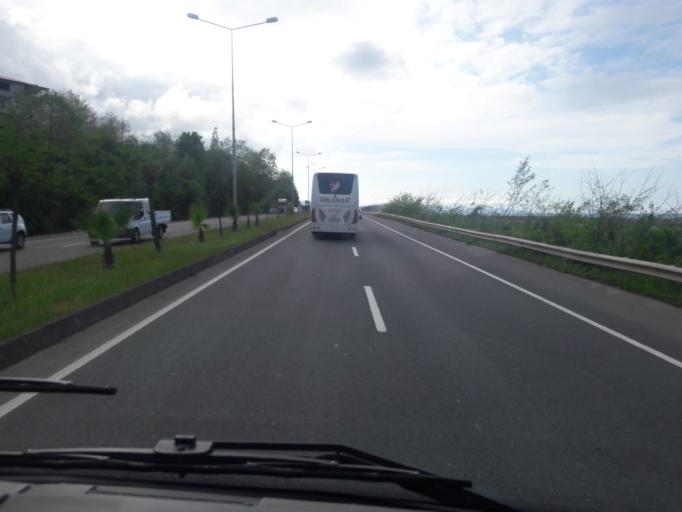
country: TR
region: Giresun
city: Piraziz
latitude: 40.9620
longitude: 38.0995
